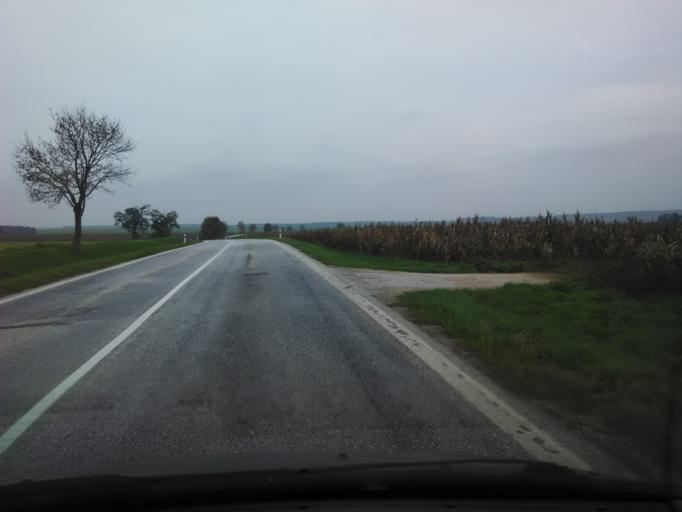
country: SK
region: Nitriansky
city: Svodin
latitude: 48.0081
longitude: 18.3775
